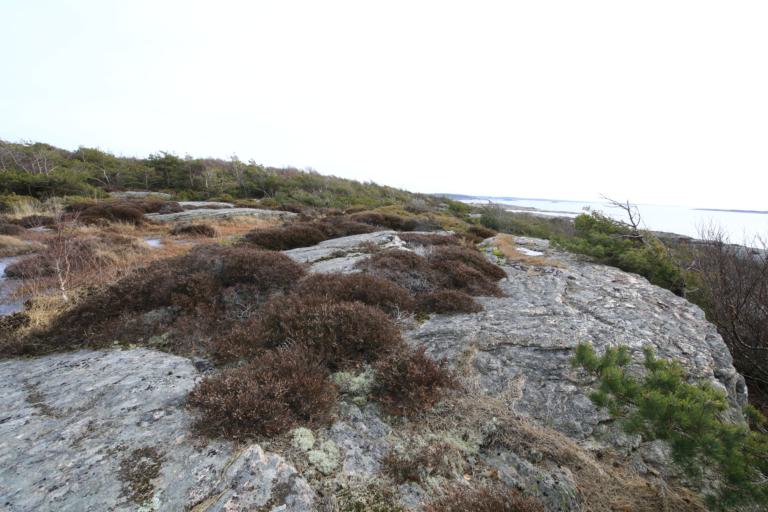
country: SE
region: Halland
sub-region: Kungsbacka Kommun
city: Frillesas
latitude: 57.2328
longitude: 12.0998
